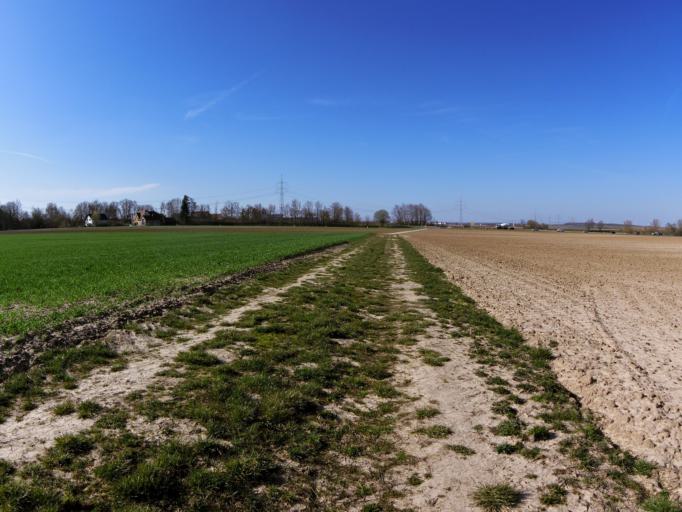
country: DE
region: Bavaria
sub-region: Regierungsbezirk Unterfranken
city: Prosselsheim
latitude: 49.8542
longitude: 10.1069
